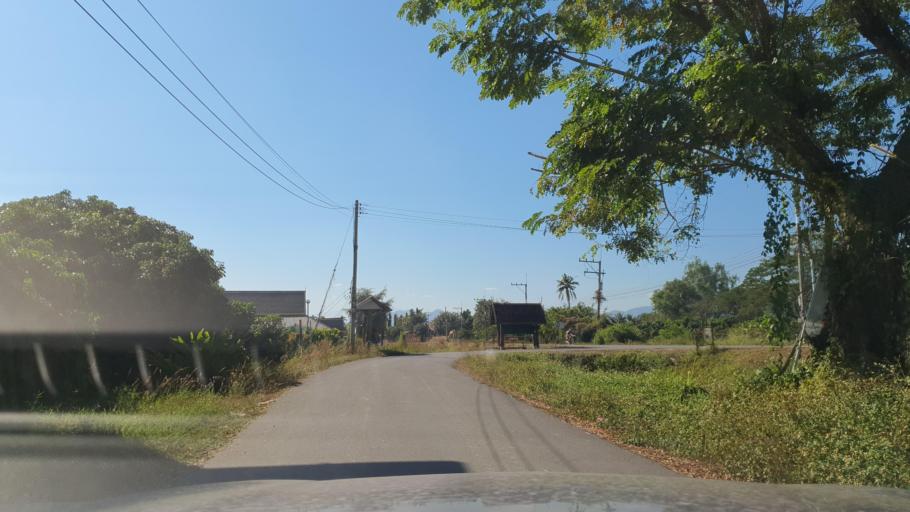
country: TH
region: Chiang Mai
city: San Pa Tong
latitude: 18.6514
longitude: 98.8672
